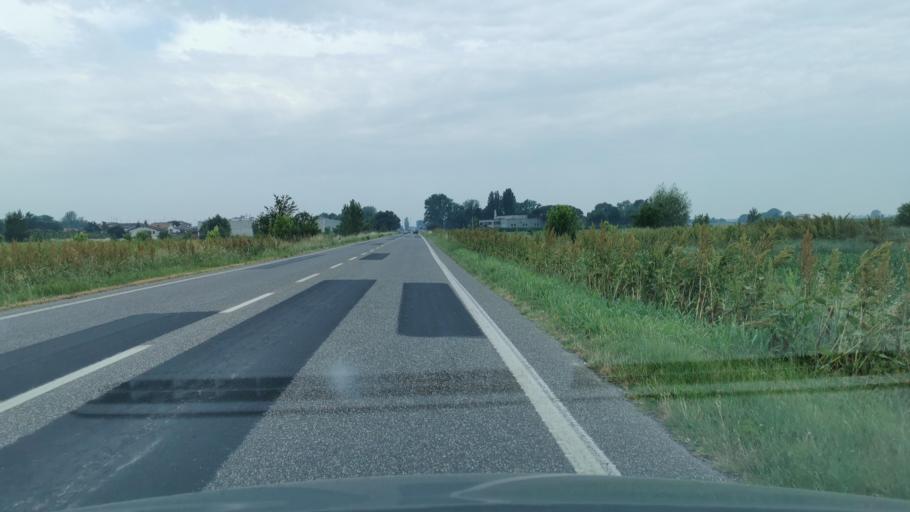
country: IT
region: Emilia-Romagna
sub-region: Provincia di Ravenna
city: Godo
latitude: 44.3963
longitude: 12.0750
